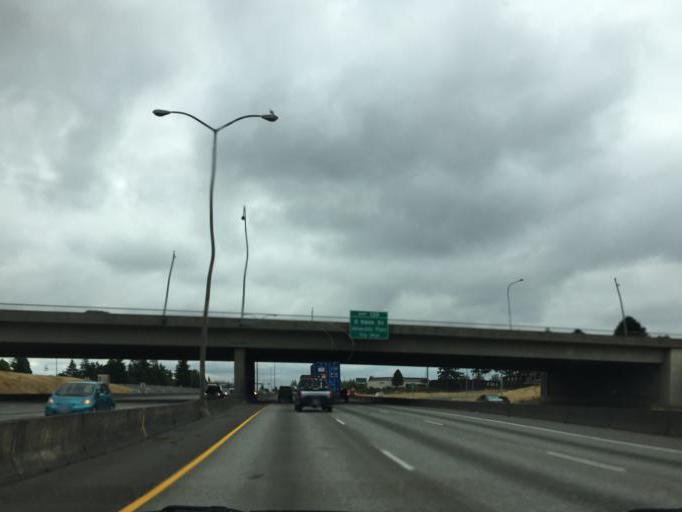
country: US
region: Washington
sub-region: Pierce County
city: Tacoma
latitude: 47.2236
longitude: -122.4635
